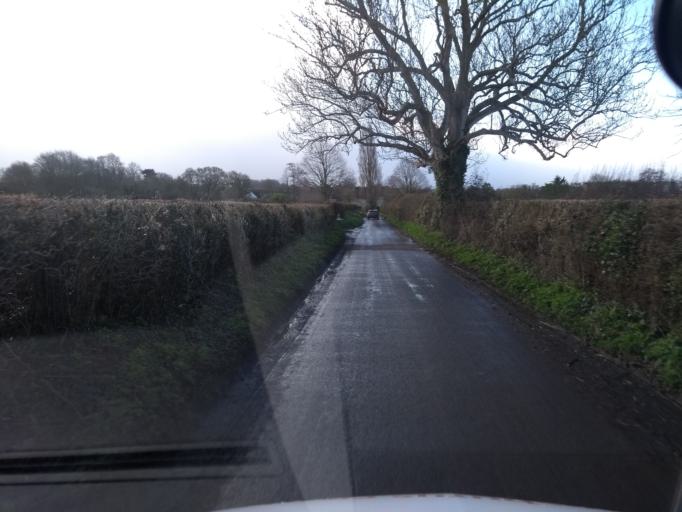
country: GB
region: England
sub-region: Dorset
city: Sherborne
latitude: 50.9976
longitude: -2.5591
